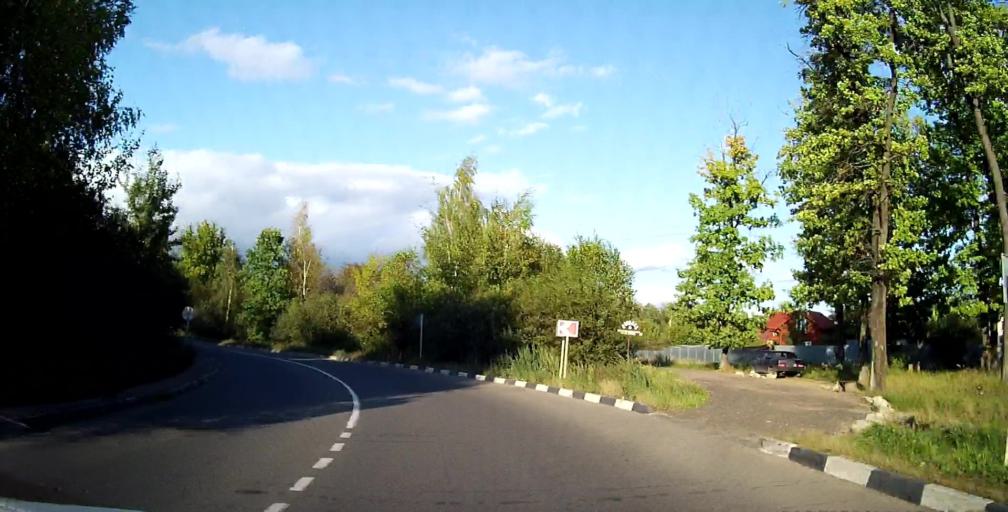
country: RU
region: Moskovskaya
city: Klimovsk
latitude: 55.3625
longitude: 37.5651
